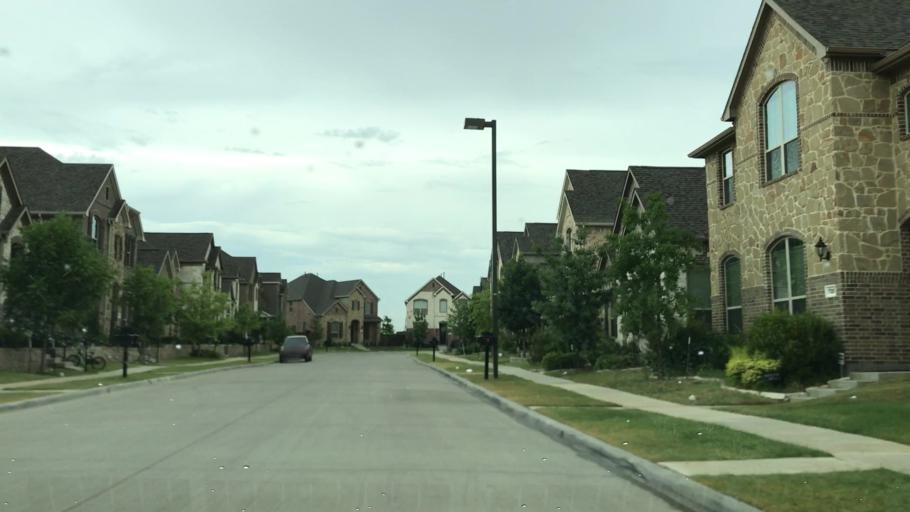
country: US
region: Texas
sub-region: Dallas County
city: Coppell
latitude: 32.9054
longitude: -96.9960
